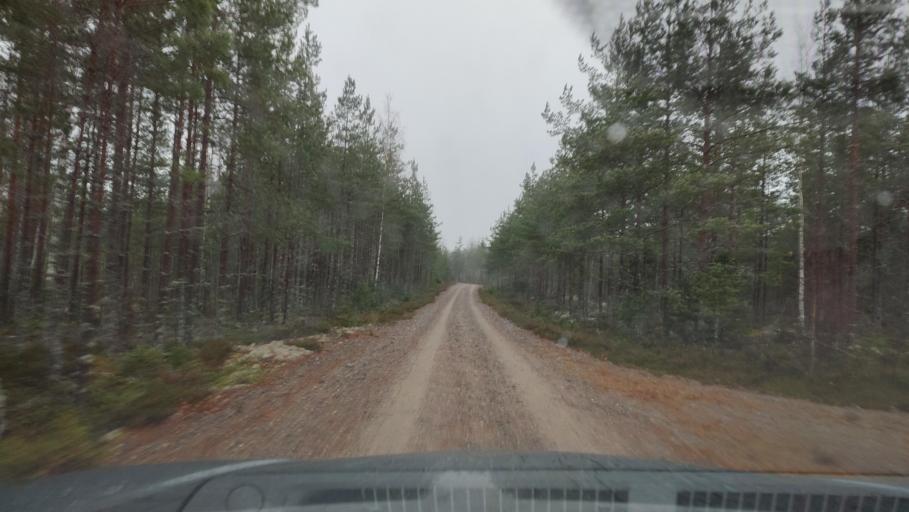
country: FI
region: Southern Ostrobothnia
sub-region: Suupohja
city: Karijoki
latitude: 62.1886
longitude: 21.7412
